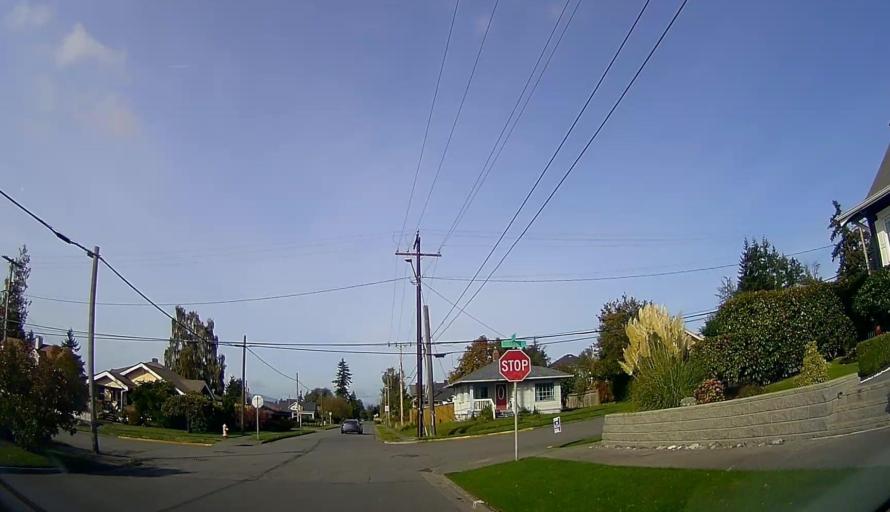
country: US
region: Washington
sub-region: Skagit County
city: Mount Vernon
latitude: 48.4240
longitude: -122.3307
